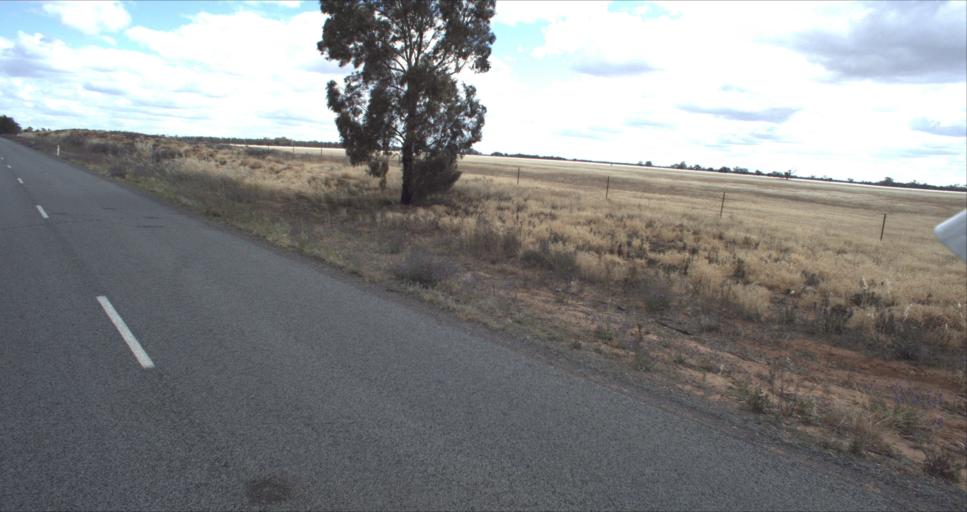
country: AU
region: New South Wales
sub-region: Leeton
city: Leeton
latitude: -34.6720
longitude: 146.3472
